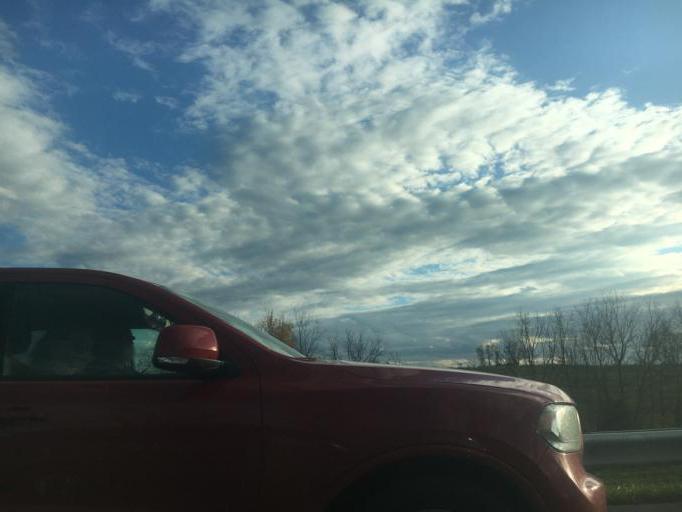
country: US
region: Virginia
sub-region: Washington County
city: Emory
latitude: 36.7697
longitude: -81.8054
